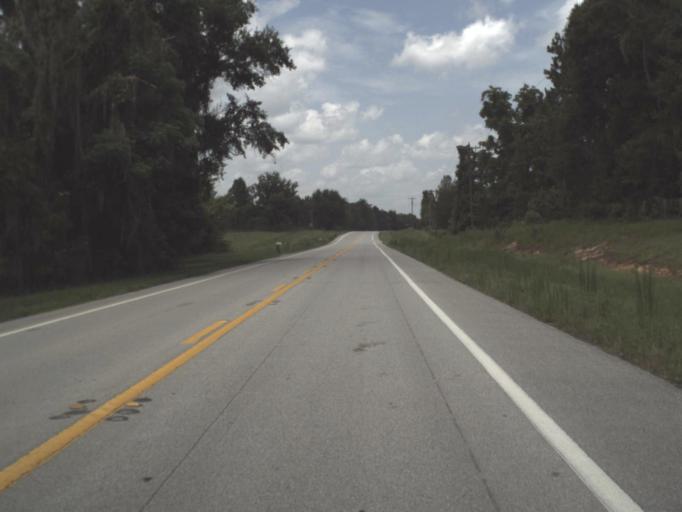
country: US
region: Florida
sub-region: Madison County
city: Madison
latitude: 30.5619
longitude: -83.4297
